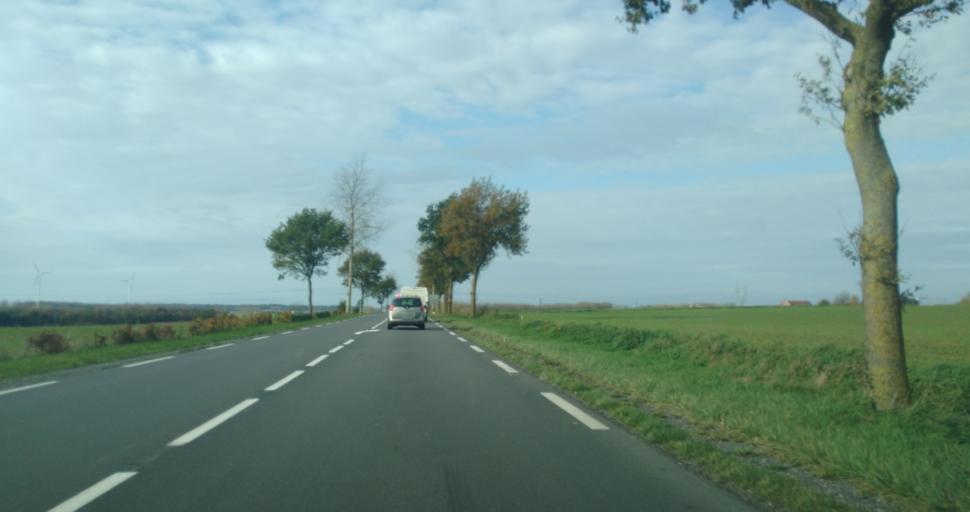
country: FR
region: Nord-Pas-de-Calais
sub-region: Departement du Pas-de-Calais
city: Savy-Berlette
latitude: 50.3509
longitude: 2.5209
